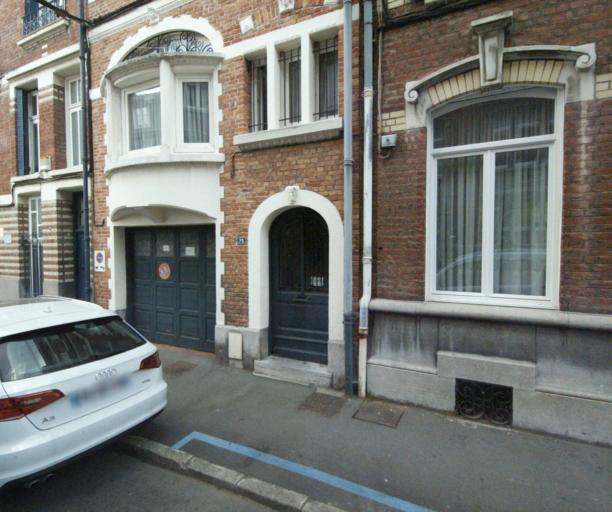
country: FR
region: Nord-Pas-de-Calais
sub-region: Departement du Nord
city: La Madeleine
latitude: 50.6501
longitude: 3.0772
